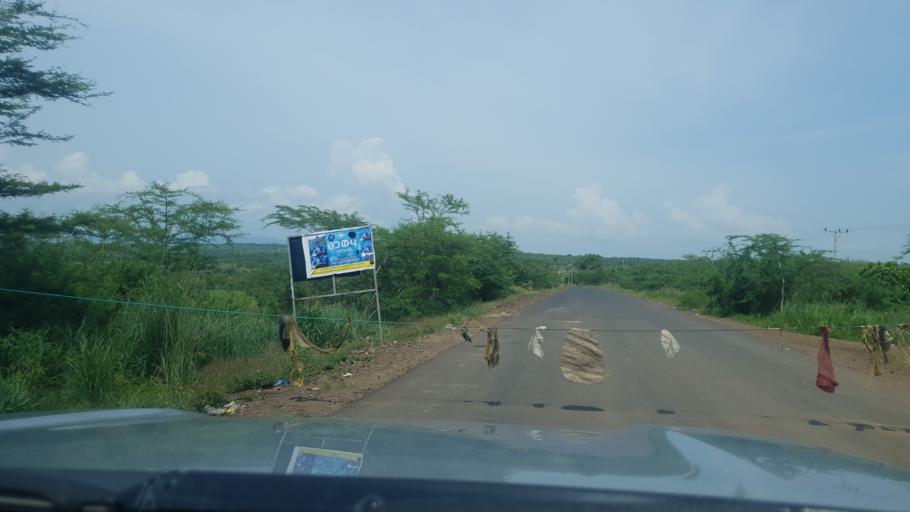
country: ET
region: Southern Nations, Nationalities, and People's Region
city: Mizan Teferi
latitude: 6.5434
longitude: 35.1755
